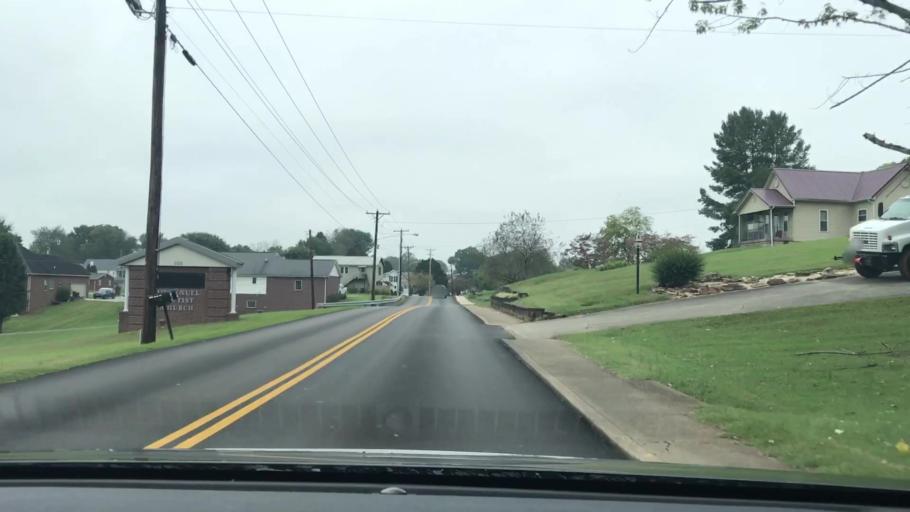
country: US
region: Kentucky
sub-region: Pulaski County
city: Somerset
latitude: 37.0883
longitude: -84.5922
